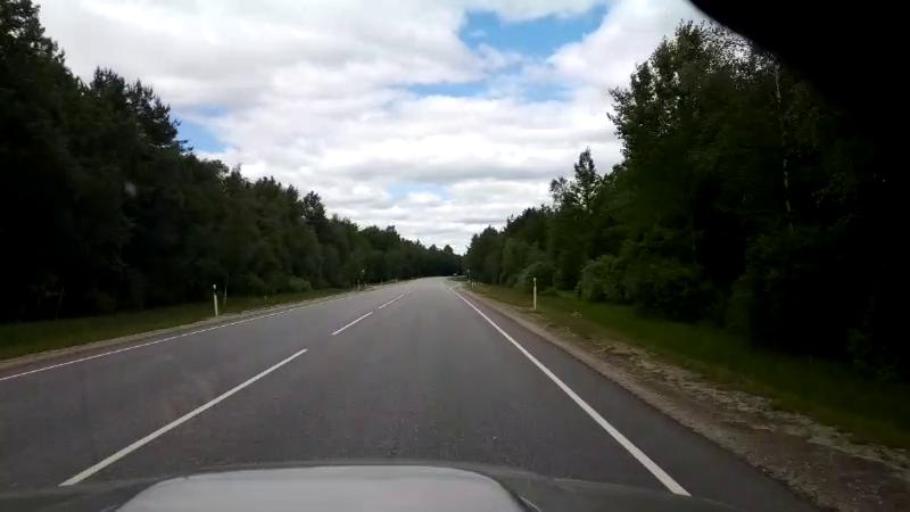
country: EE
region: Raplamaa
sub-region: Maerjamaa vald
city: Marjamaa
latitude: 58.9492
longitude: 24.4677
